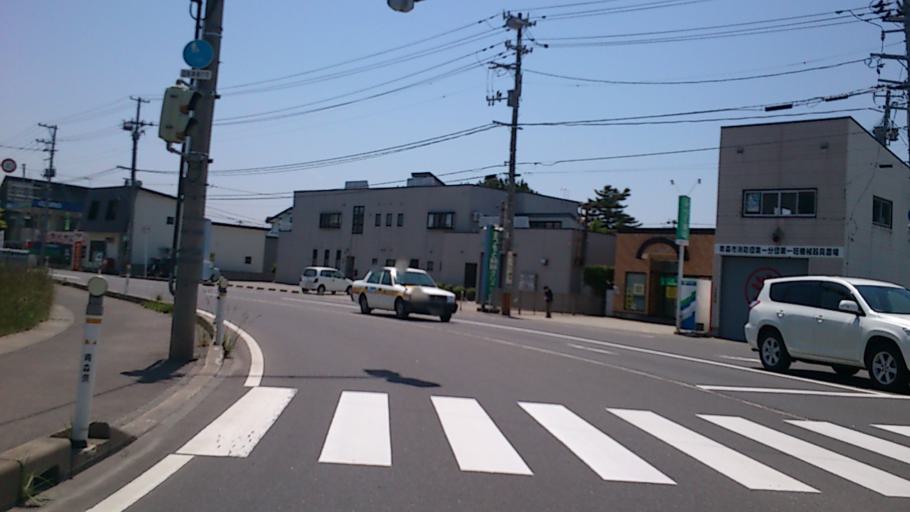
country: JP
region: Aomori
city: Aomori Shi
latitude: 40.8336
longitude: 140.7232
